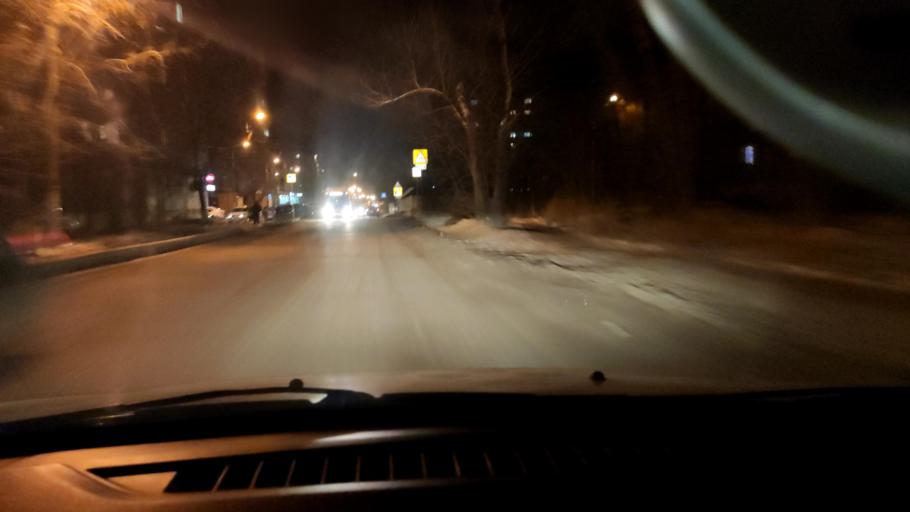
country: RU
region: Perm
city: Overyata
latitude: 58.0265
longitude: 55.8438
